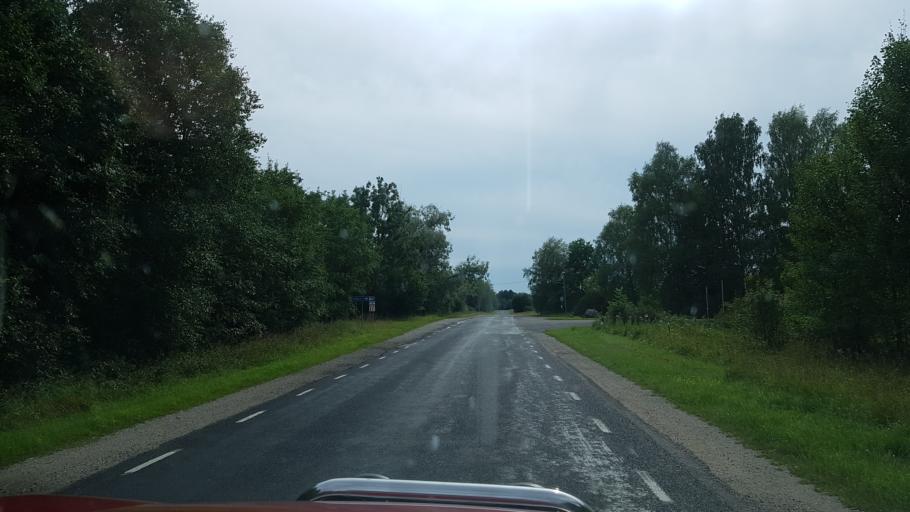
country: EE
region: Laeaene
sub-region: Ridala Parish
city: Uuemoisa
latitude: 59.0167
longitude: 23.7933
